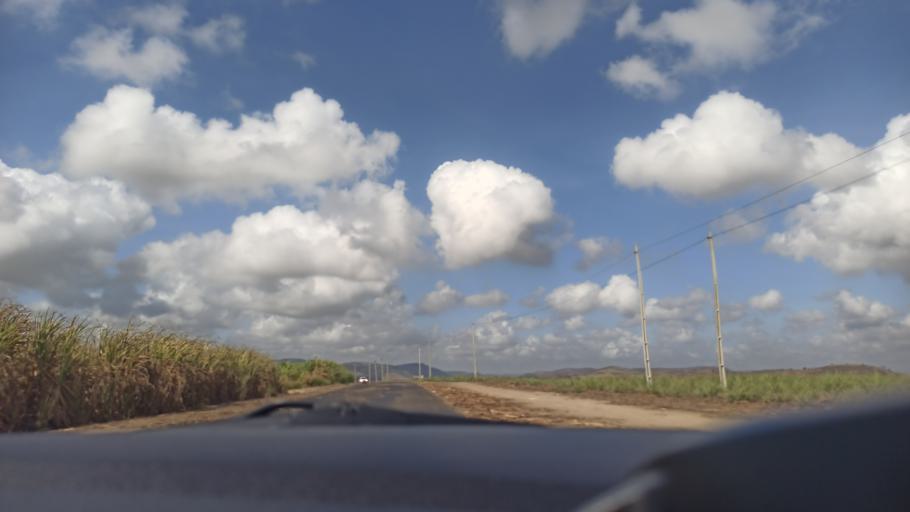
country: BR
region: Paraiba
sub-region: Juripiranga
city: Juripiranga
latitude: -7.3863
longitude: -35.2503
